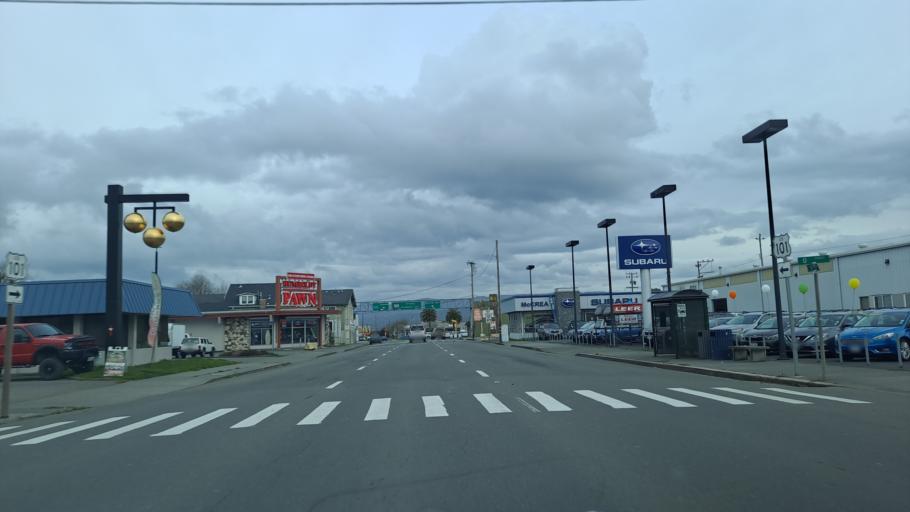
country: US
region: California
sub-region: Humboldt County
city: Eureka
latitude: 40.8033
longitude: -124.1563
